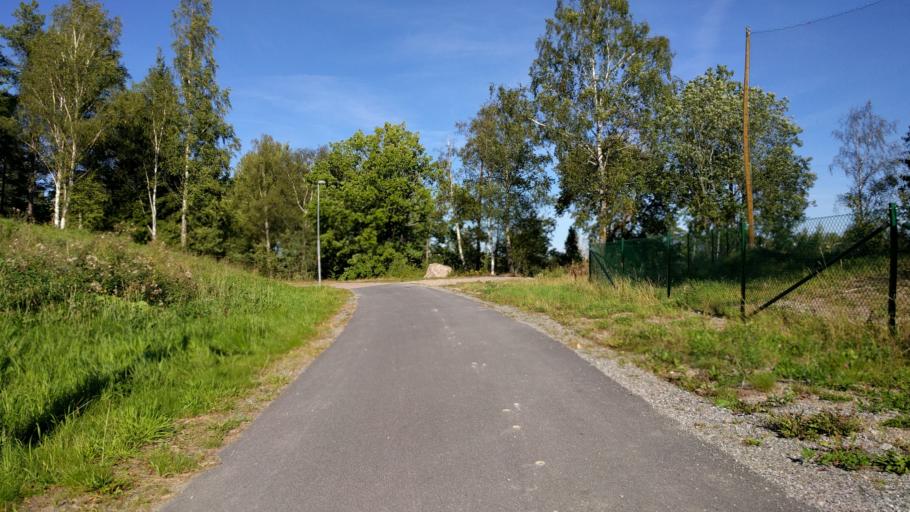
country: SE
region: Stockholm
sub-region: Taby Kommun
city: Taby
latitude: 59.4747
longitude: 18.1214
